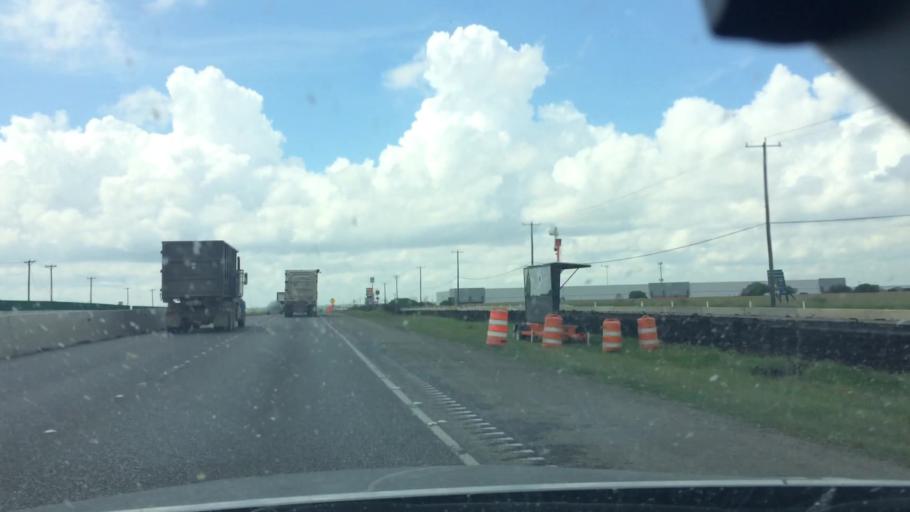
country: US
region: Texas
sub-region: Bexar County
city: Kirby
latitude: 29.4480
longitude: -98.3523
